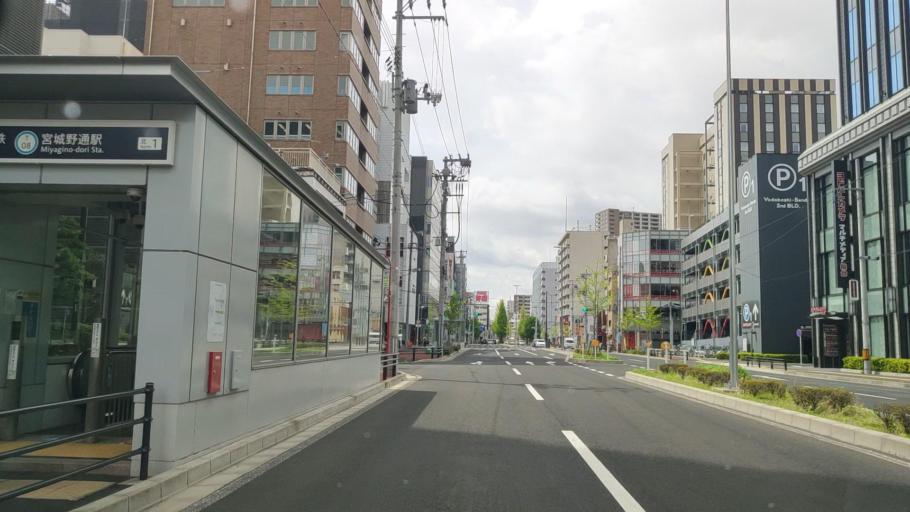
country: JP
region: Miyagi
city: Sendai-shi
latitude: 38.2593
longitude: 140.8861
